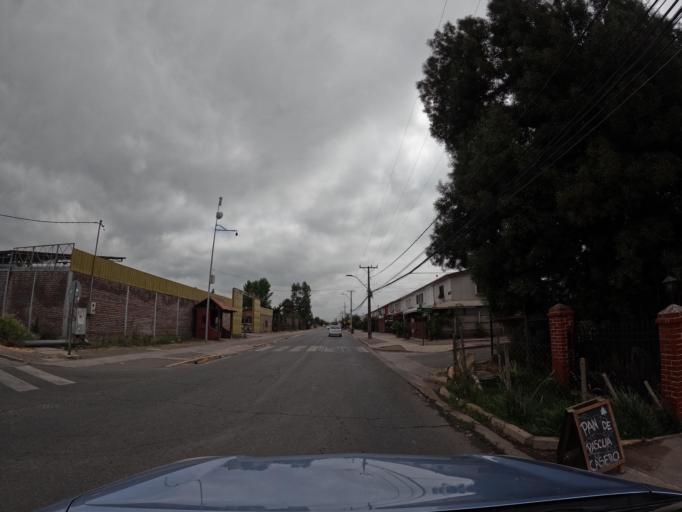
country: CL
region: O'Higgins
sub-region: Provincia de Colchagua
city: Chimbarongo
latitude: -34.7166
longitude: -71.0493
